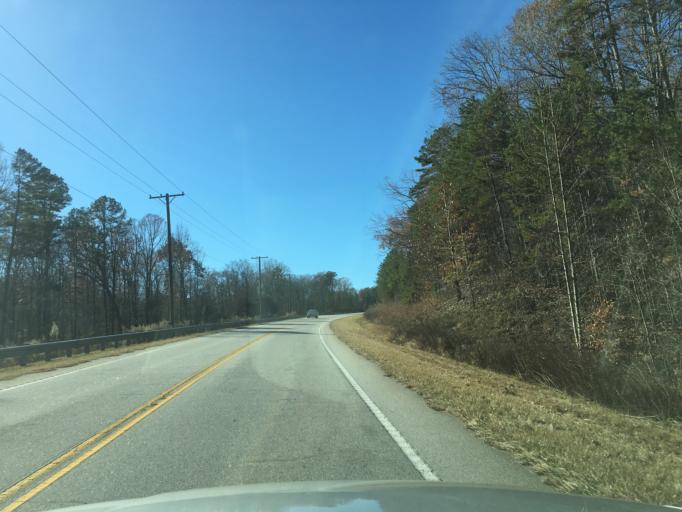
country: US
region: South Carolina
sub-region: Oconee County
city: Walhalla
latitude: 34.9146
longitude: -82.9166
